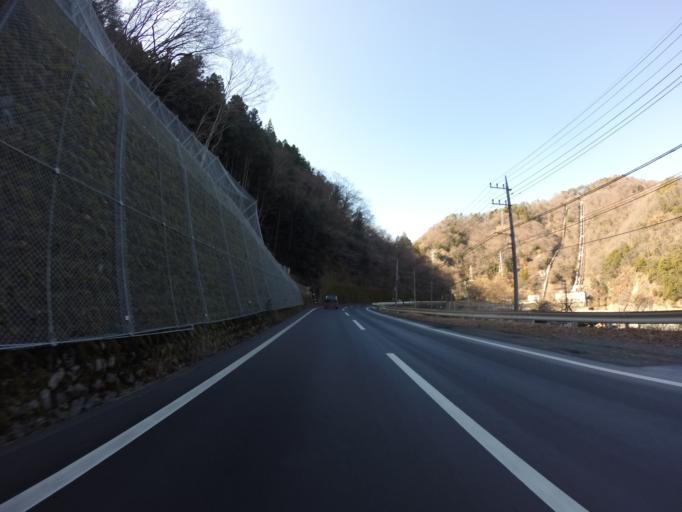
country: JP
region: Yamanashi
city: Ryuo
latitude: 35.4247
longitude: 138.4083
